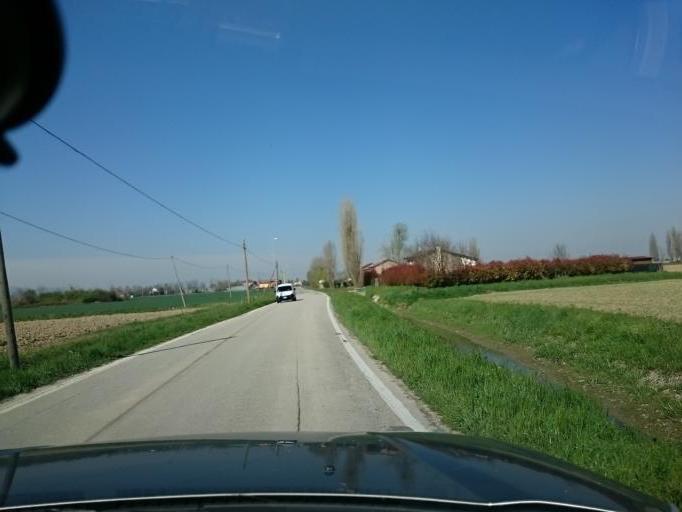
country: IT
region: Veneto
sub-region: Provincia di Padova
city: Ponte San Nicolo
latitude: 45.3452
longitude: 11.9225
